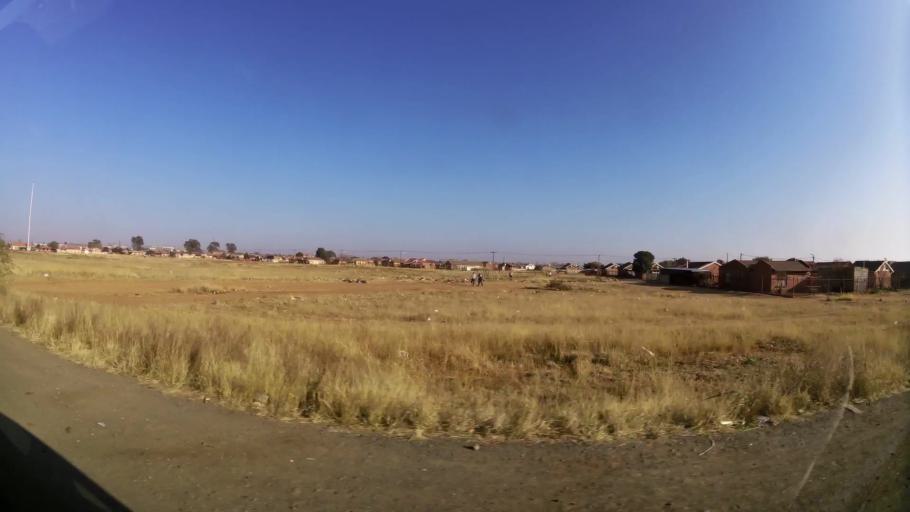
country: ZA
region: Orange Free State
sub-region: Mangaung Metropolitan Municipality
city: Bloemfontein
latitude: -29.1548
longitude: 26.2644
